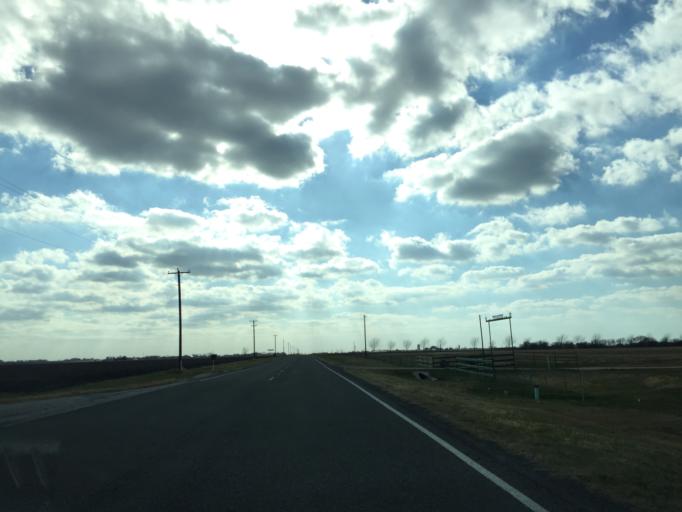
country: US
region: Texas
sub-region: Williamson County
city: Granger
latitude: 30.6621
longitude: -97.3683
